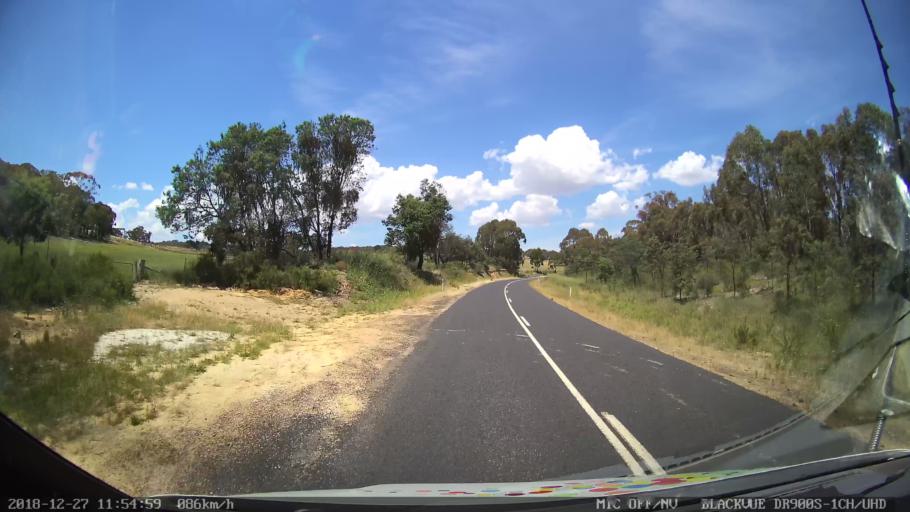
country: AU
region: New South Wales
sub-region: Blayney
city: Blayney
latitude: -33.6820
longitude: 149.4010
